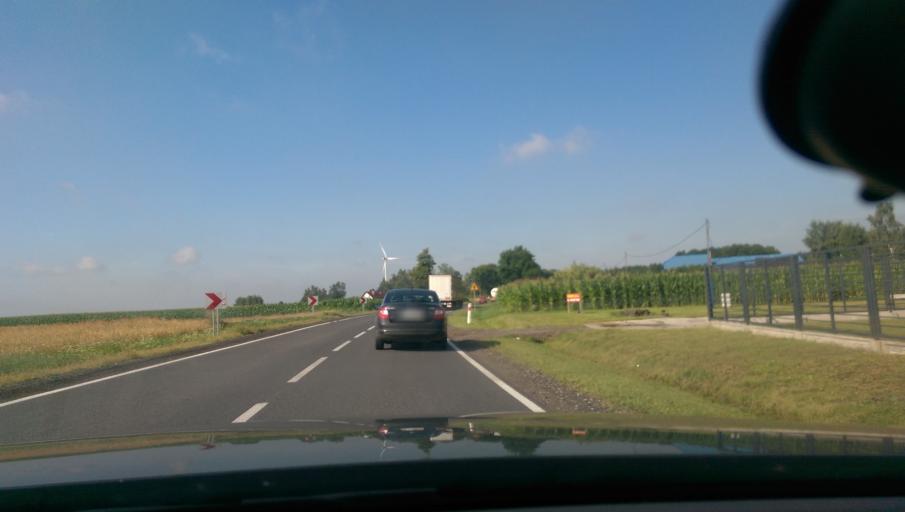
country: PL
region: Masovian Voivodeship
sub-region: Powiat plonski
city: Plonsk
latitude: 52.6475
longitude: 20.4234
